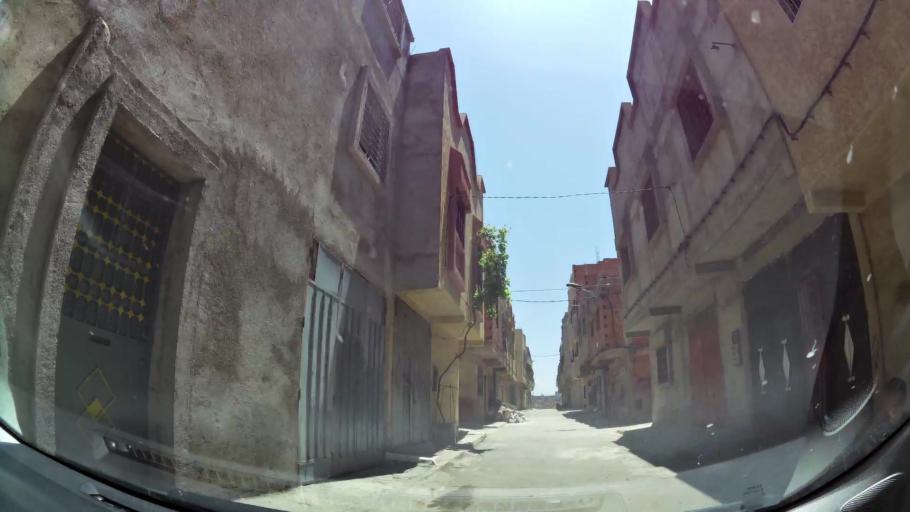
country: MA
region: Oriental
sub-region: Oujda-Angad
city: Oujda
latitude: 34.6866
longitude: -1.9527
